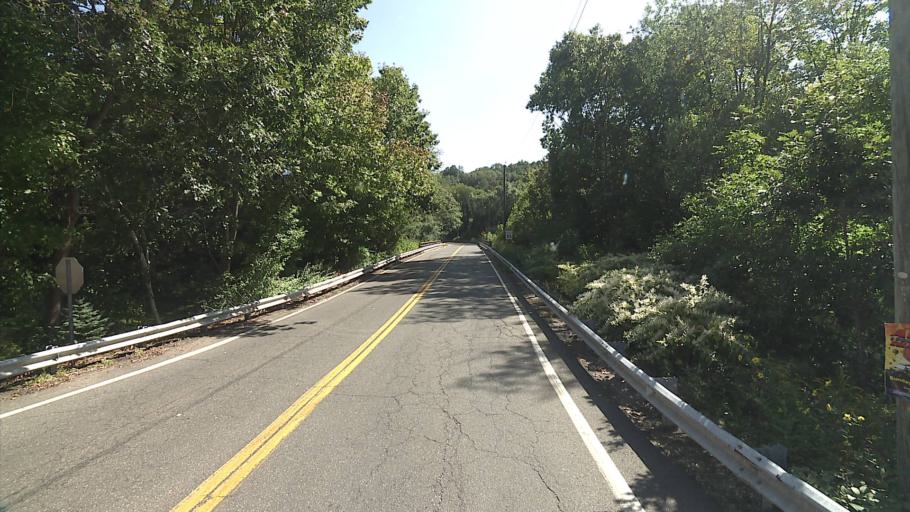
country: US
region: Connecticut
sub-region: Litchfield County
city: Thomaston
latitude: 41.6872
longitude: -73.0668
